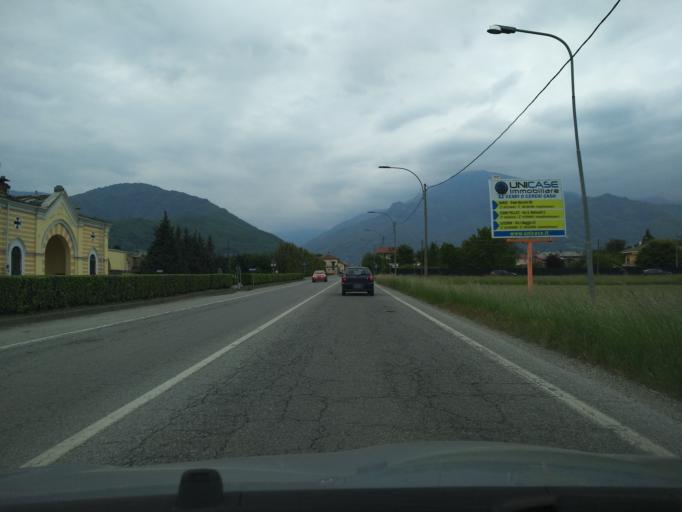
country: IT
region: Piedmont
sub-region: Provincia di Torino
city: Airali
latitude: 44.8122
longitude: 7.2607
